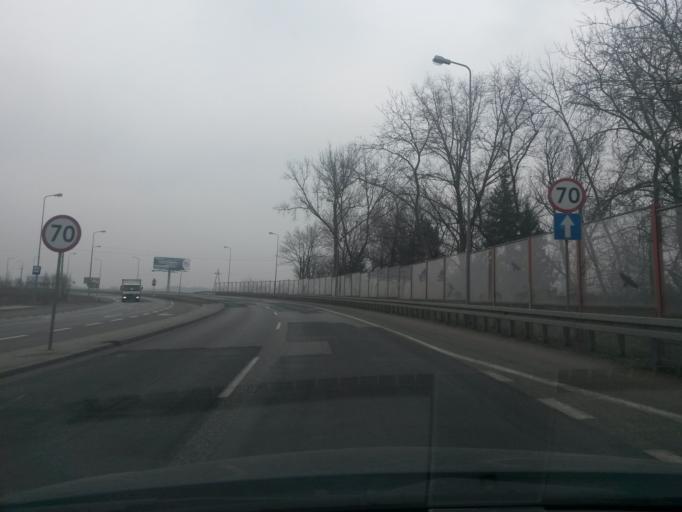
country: PL
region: Masovian Voivodeship
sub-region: Powiat legionowski
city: Bialobrzegi
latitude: 52.4659
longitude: 21.0285
